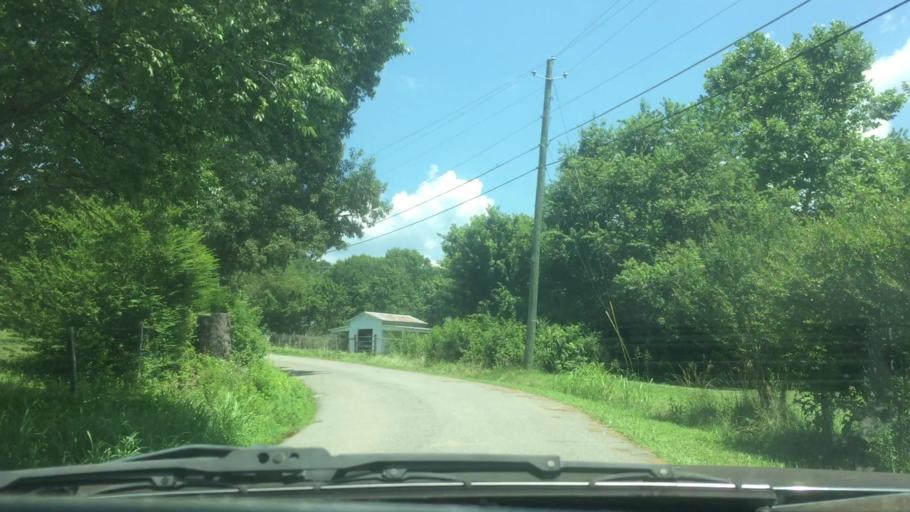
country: US
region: Georgia
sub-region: Bartow County
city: Rydal
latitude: 34.3269
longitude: -84.7061
